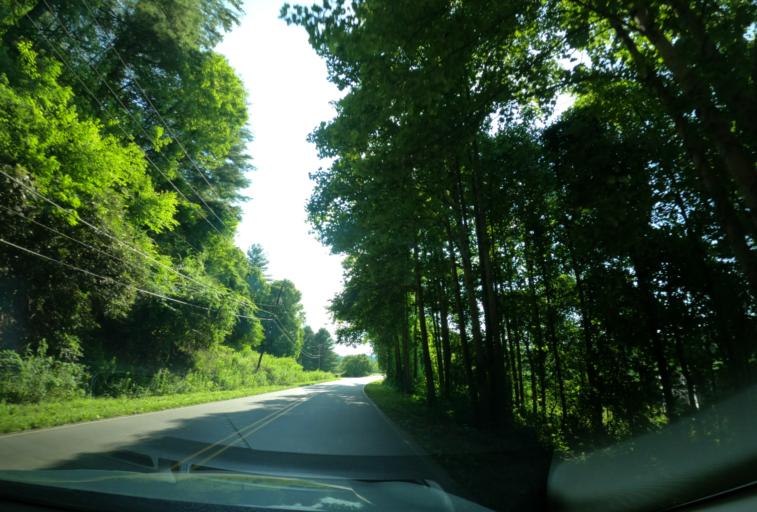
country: US
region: North Carolina
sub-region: Transylvania County
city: Brevard
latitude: 35.2511
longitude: -82.6761
